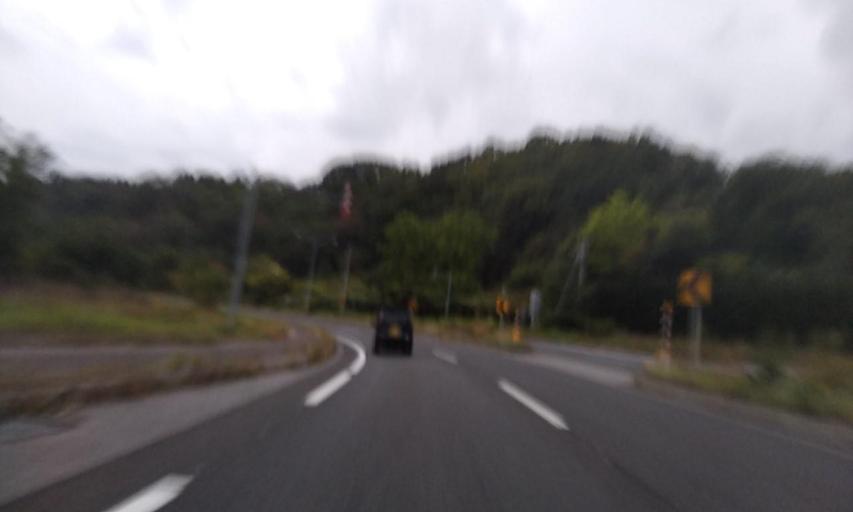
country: JP
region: Hokkaido
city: Abashiri
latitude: 44.0122
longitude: 144.2800
